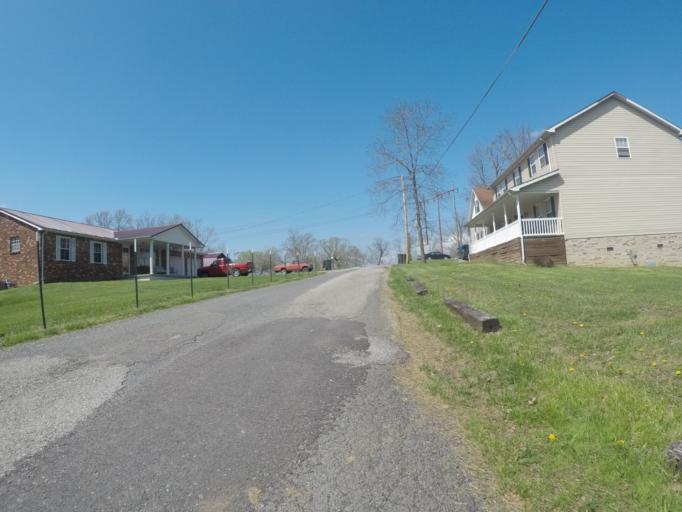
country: US
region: Ohio
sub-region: Lawrence County
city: Burlington
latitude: 38.3885
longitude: -82.5387
